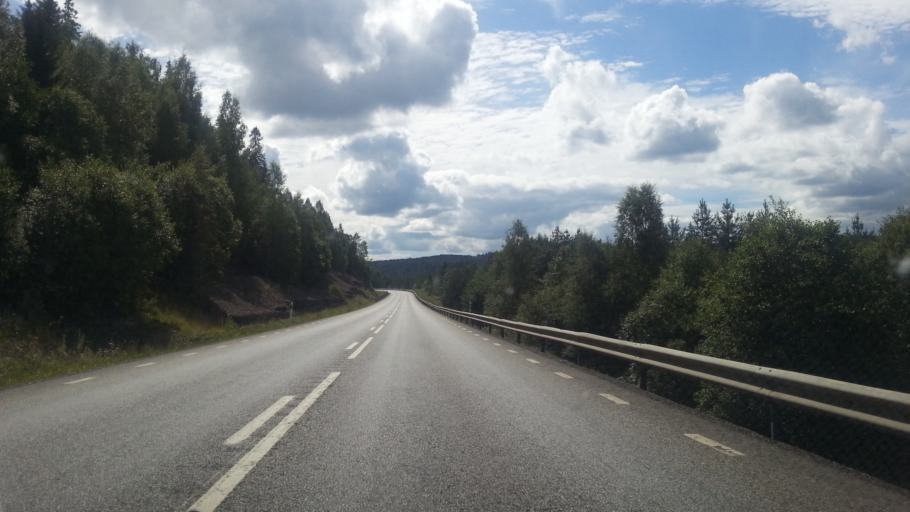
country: SE
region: OErebro
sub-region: Ljusnarsbergs Kommun
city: Kopparberg
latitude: 59.8572
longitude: 15.0601
